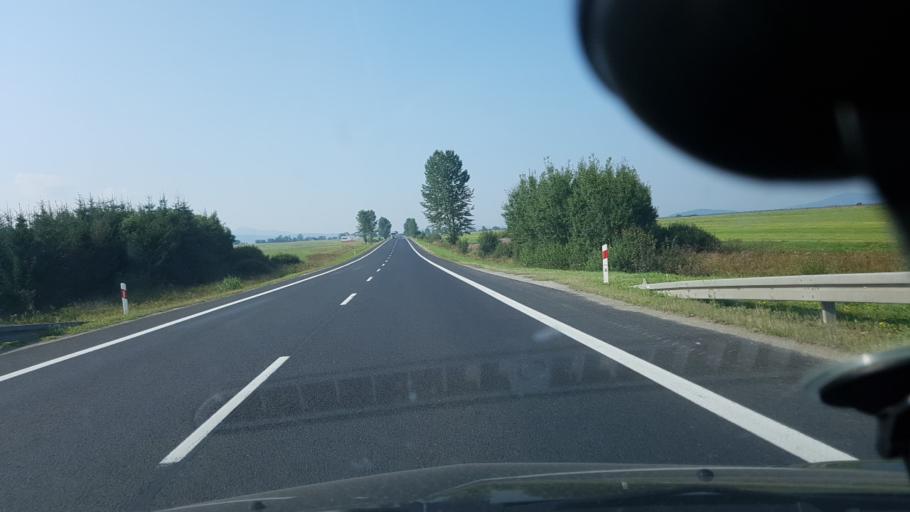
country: PL
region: Lesser Poland Voivodeship
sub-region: Powiat nowotarski
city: Chyzne
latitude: 49.4411
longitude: 19.6822
